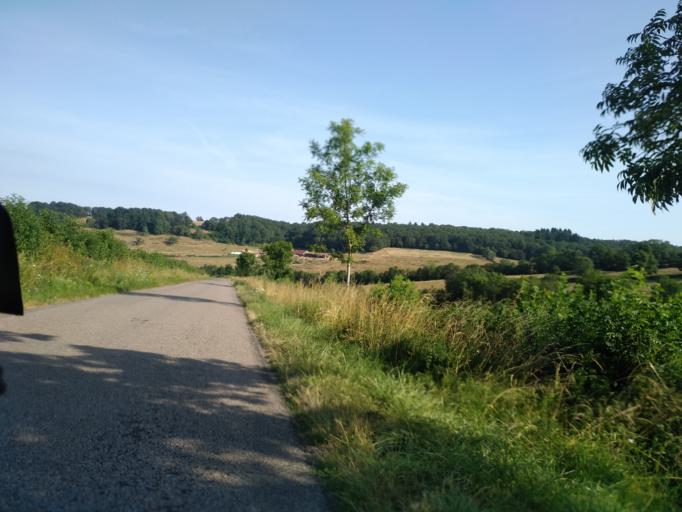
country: FR
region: Bourgogne
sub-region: Departement de Saone-et-Loire
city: Marcigny
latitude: 46.2566
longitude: 4.1106
